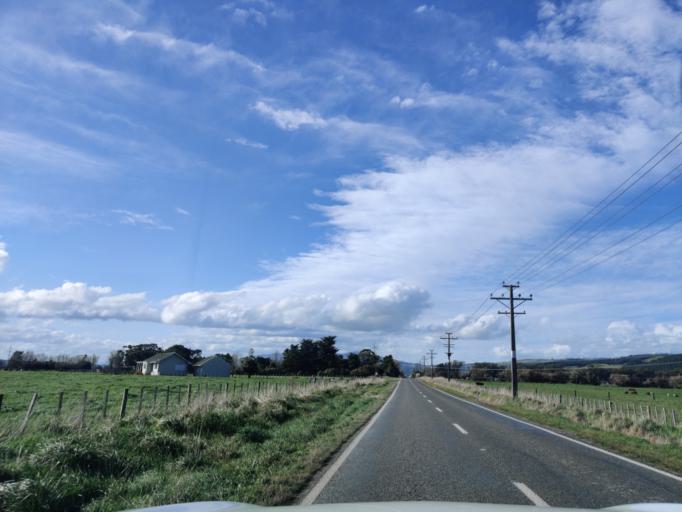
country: NZ
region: Manawatu-Wanganui
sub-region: Palmerston North City
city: Palmerston North
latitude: -40.3468
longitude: 175.7057
